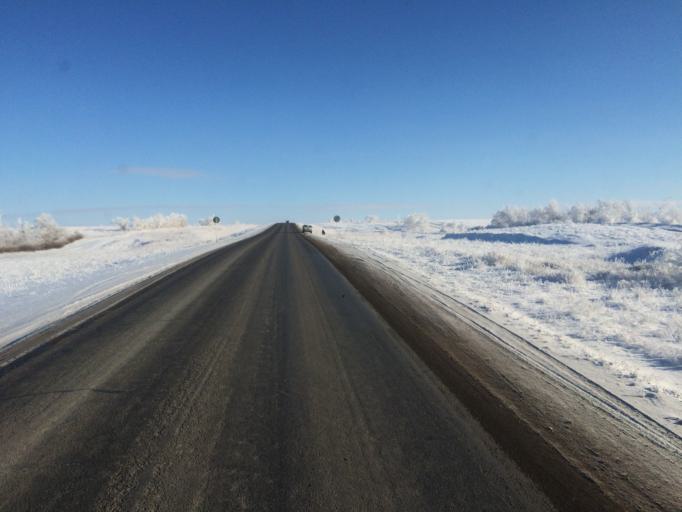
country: KZ
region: Aqtoebe
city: Batamshinskiy
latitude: 50.2842
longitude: 57.7858
